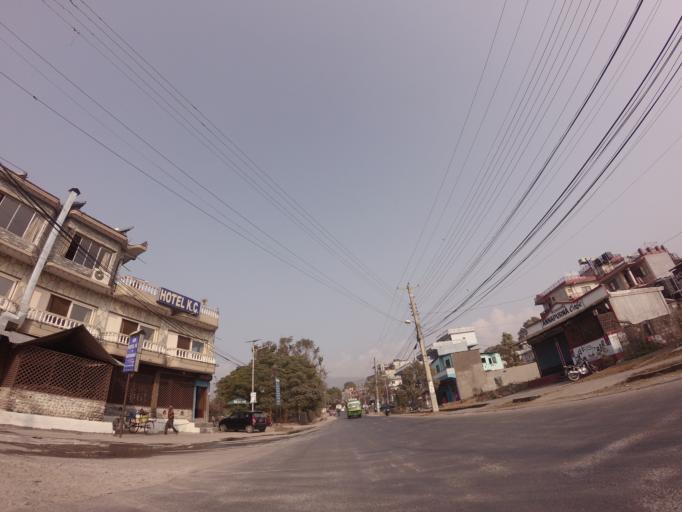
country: NP
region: Western Region
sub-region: Gandaki Zone
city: Pokhara
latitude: 28.1970
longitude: 83.9698
